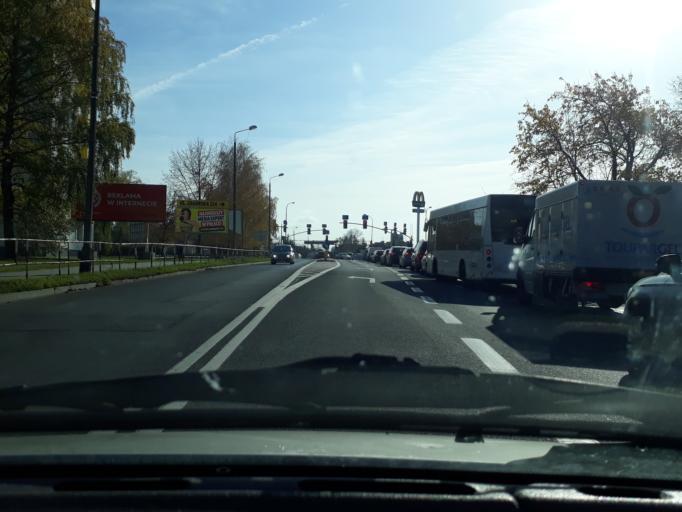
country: PL
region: Silesian Voivodeship
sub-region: Powiat tarnogorski
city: Tarnowskie Gory
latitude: 50.4326
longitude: 18.8656
